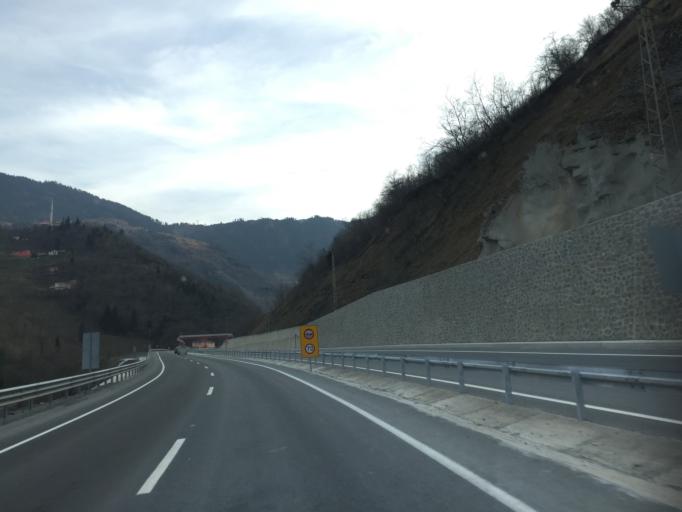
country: TR
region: Trabzon
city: Macka
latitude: 40.7633
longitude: 39.5628
